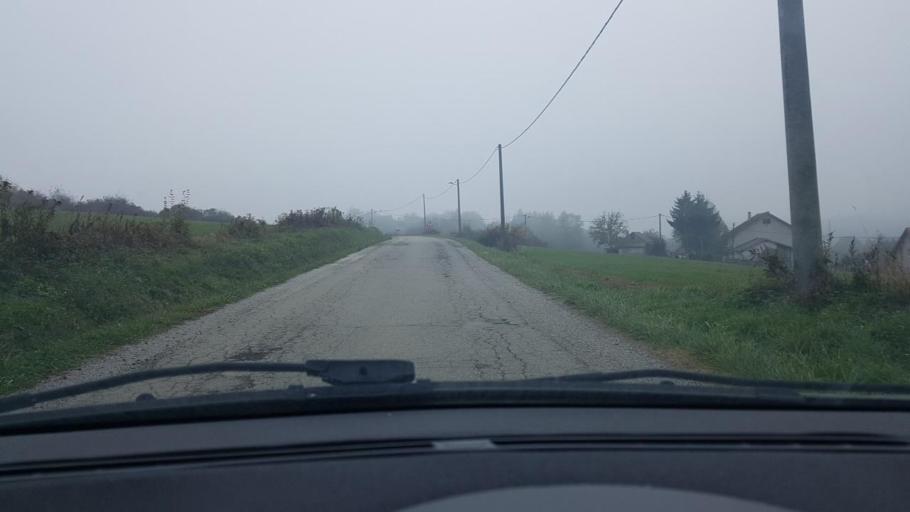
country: HR
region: Varazdinska
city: Ivanec
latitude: 46.1263
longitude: 16.1841
